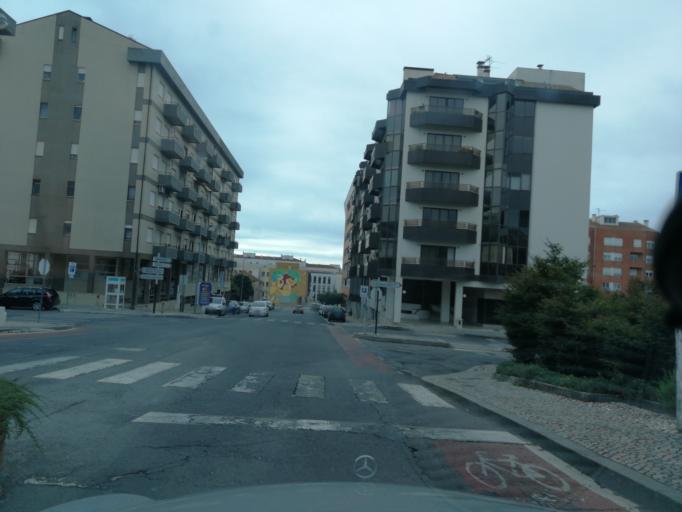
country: PT
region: Aveiro
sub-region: Agueda
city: Agueda
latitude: 40.5776
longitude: -8.4471
